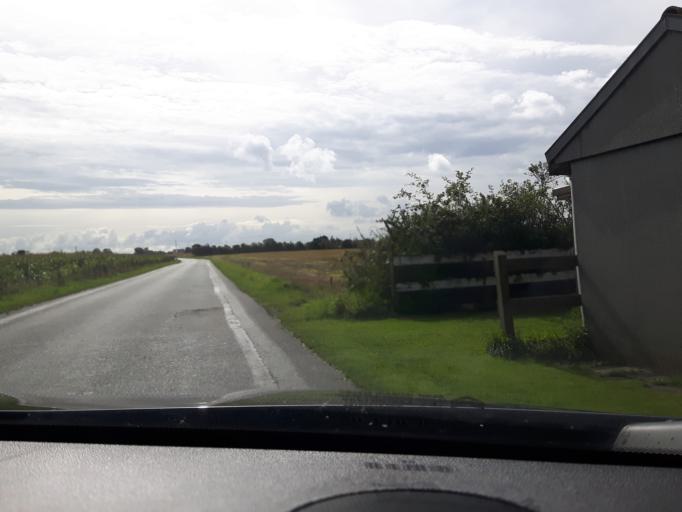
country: DK
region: South Denmark
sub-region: Fredericia Kommune
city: Fredericia
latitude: 55.6074
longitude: 9.7686
